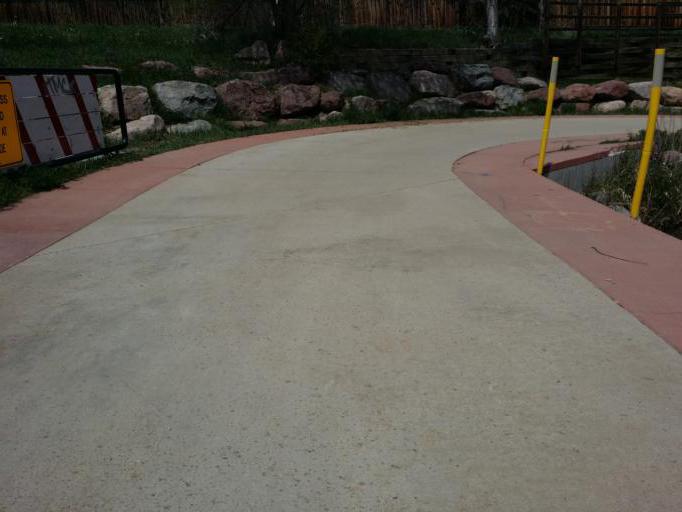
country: US
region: Colorado
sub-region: Boulder County
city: Boulder
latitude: 40.0041
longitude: -105.2401
